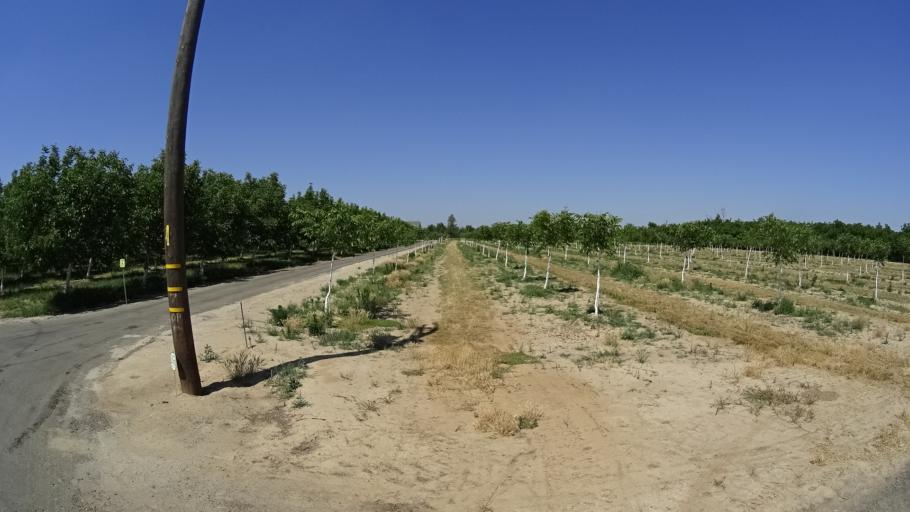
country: US
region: California
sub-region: Fresno County
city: Kingsburg
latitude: 36.4661
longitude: -119.5733
